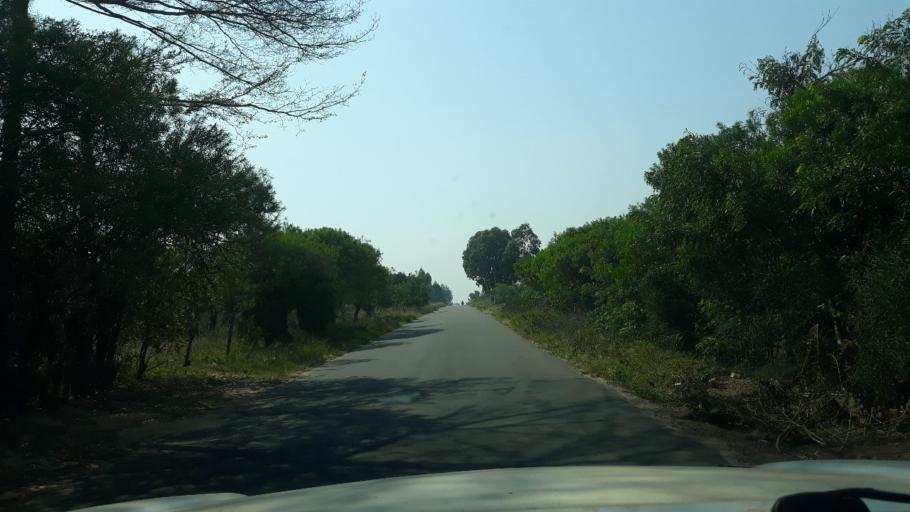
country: CD
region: South Kivu
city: Uvira
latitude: -3.2241
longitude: 29.1656
